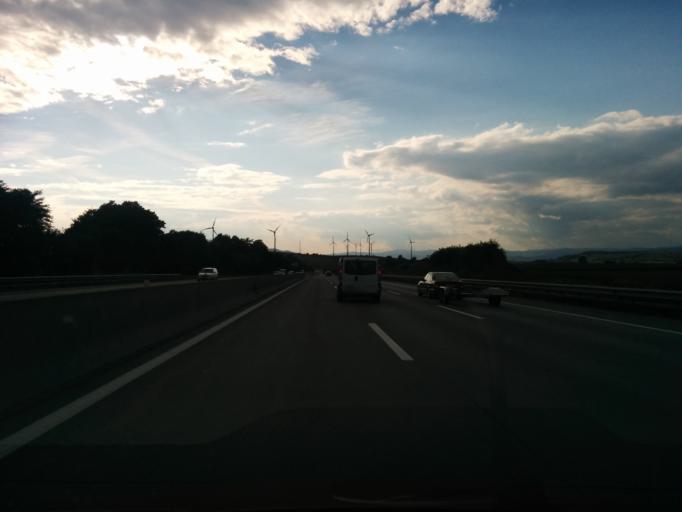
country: AT
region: Lower Austria
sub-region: Politischer Bezirk Sankt Polten
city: Sankt Margarethen an der Sierning
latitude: 48.1689
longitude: 15.4881
